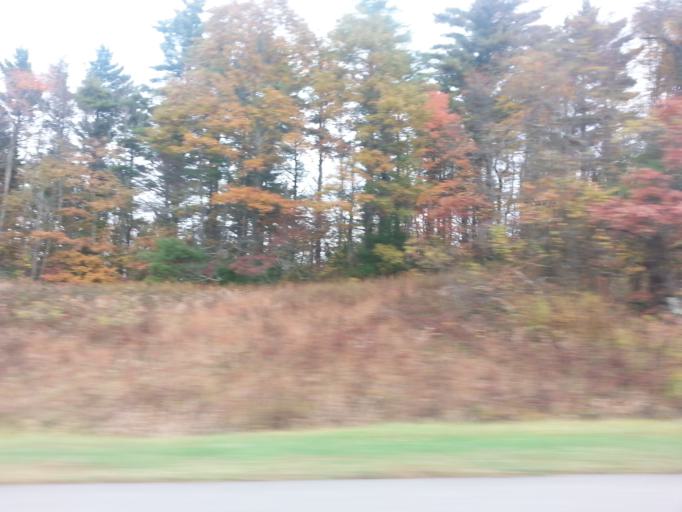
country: US
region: North Carolina
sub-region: Ashe County
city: Jefferson
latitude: 36.3327
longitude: -81.3746
